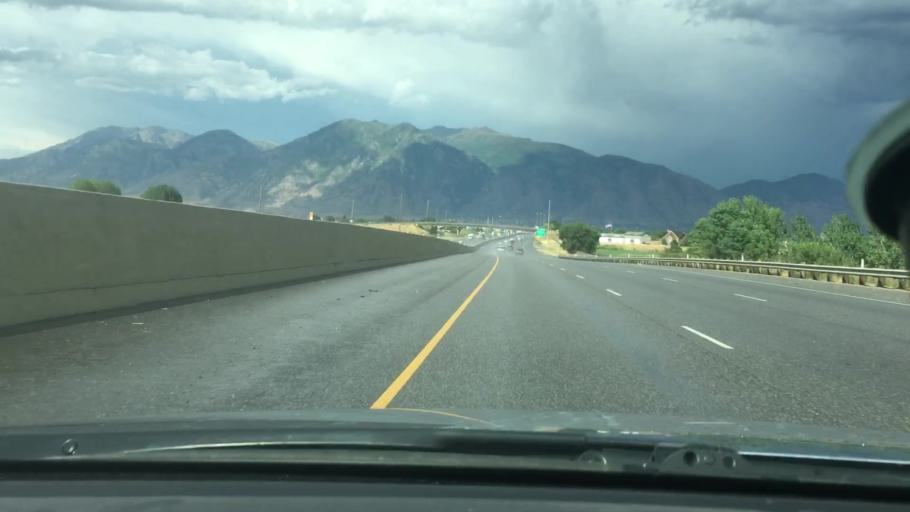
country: US
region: Utah
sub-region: Utah County
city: Spanish Fork
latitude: 40.1105
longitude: -111.6738
